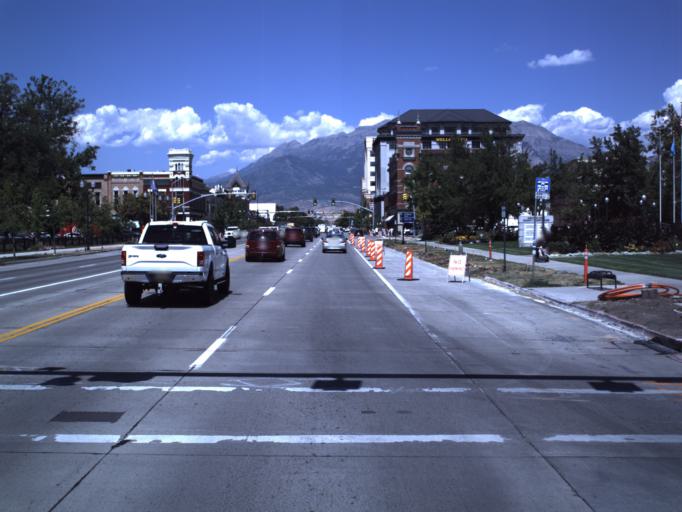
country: US
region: Utah
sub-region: Utah County
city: Provo
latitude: 40.2324
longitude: -111.6586
